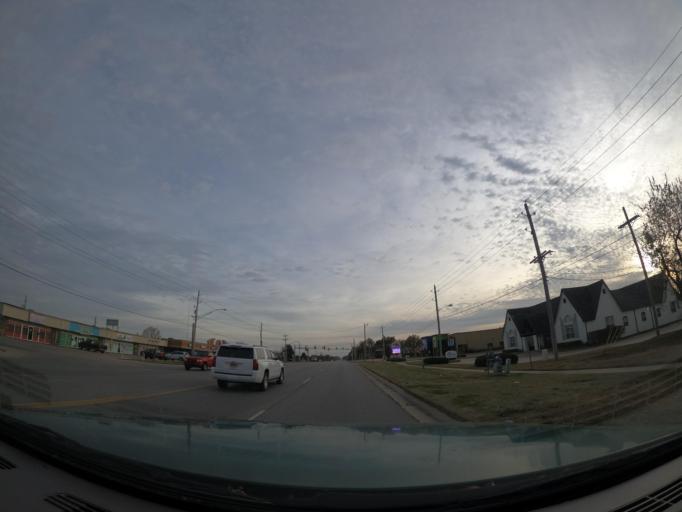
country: US
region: Oklahoma
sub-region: Tulsa County
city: Broken Arrow
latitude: 36.0556
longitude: -95.8154
